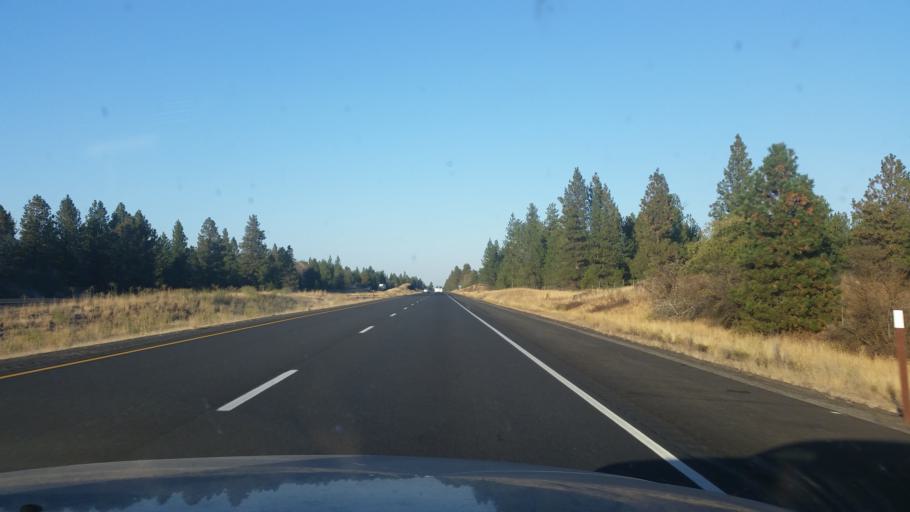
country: US
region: Washington
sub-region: Spokane County
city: Medical Lake
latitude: 47.4675
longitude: -117.7446
